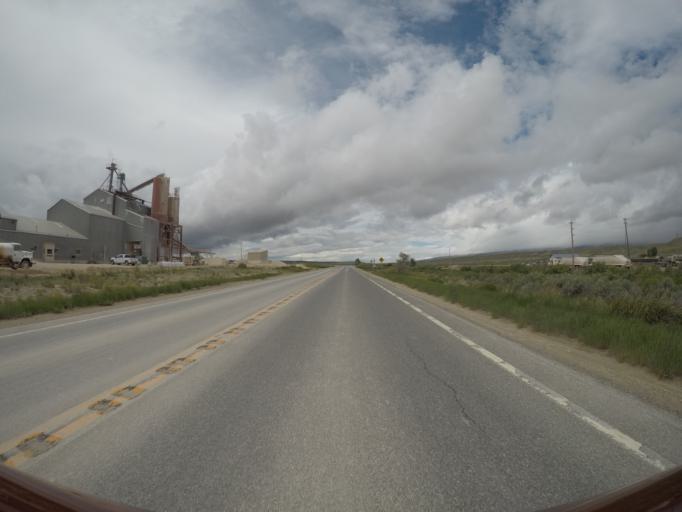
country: US
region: Wyoming
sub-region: Park County
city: Powell
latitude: 45.0576
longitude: -108.6573
